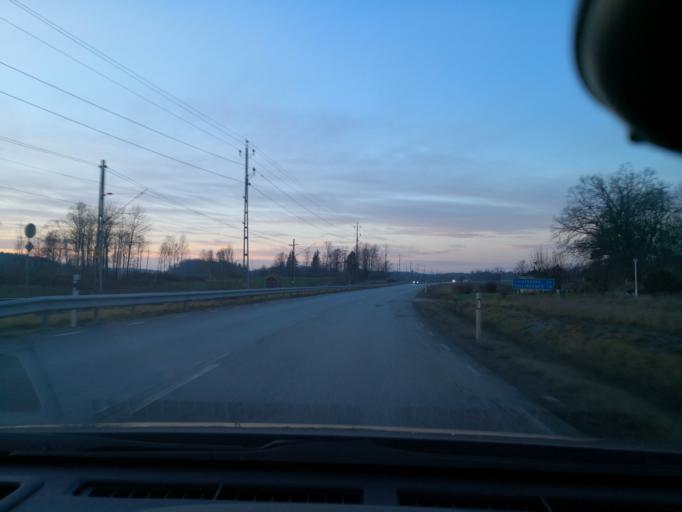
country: SE
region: Vaestmanland
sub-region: Arboga Kommun
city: Arboga
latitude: 59.4039
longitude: 15.8080
